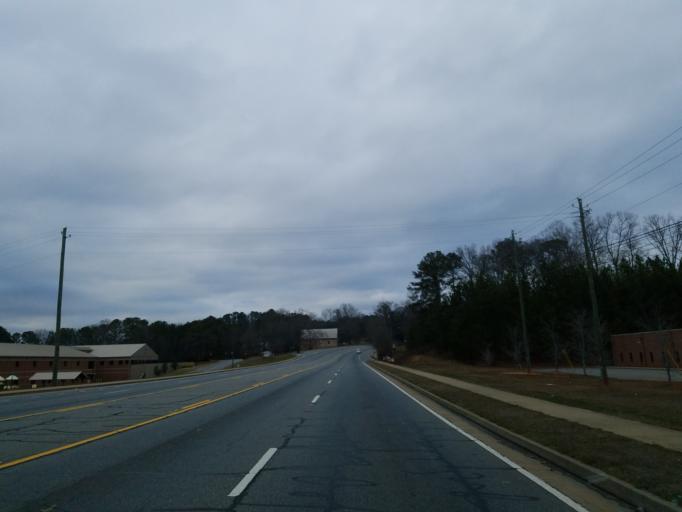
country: US
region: Georgia
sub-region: Cherokee County
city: Canton
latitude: 34.2350
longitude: -84.4999
